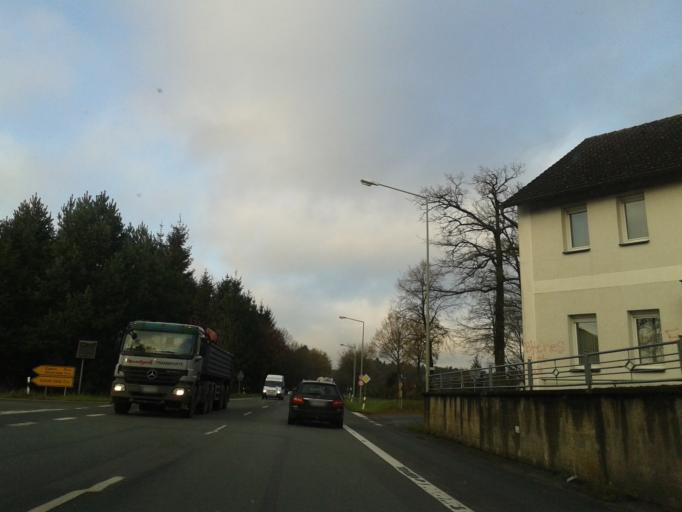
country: DE
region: North Rhine-Westphalia
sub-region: Regierungsbezirk Detmold
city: Augustdorf
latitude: 51.8781
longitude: 8.6748
